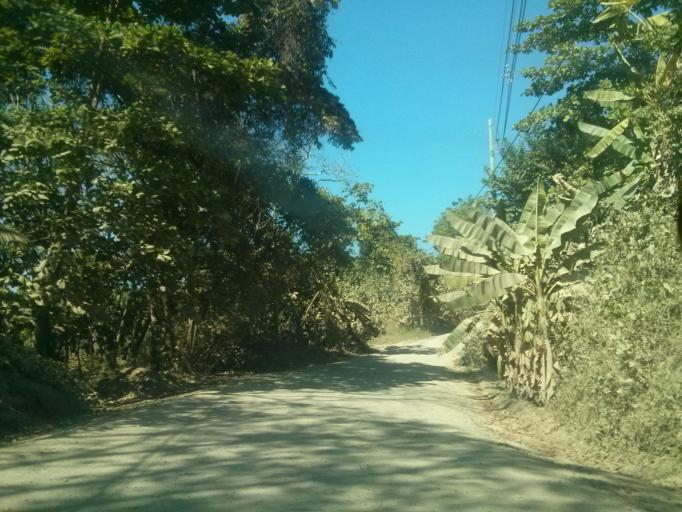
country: CR
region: Guanacaste
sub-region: Canton de Nandayure
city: Bejuco
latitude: 9.6549
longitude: -85.1813
